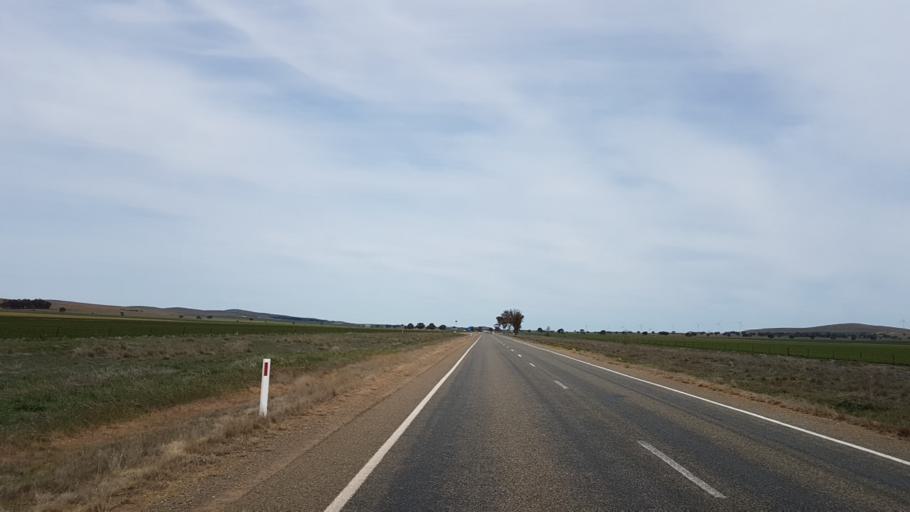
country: AU
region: South Australia
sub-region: Northern Areas
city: Jamestown
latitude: -33.0526
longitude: 138.6179
